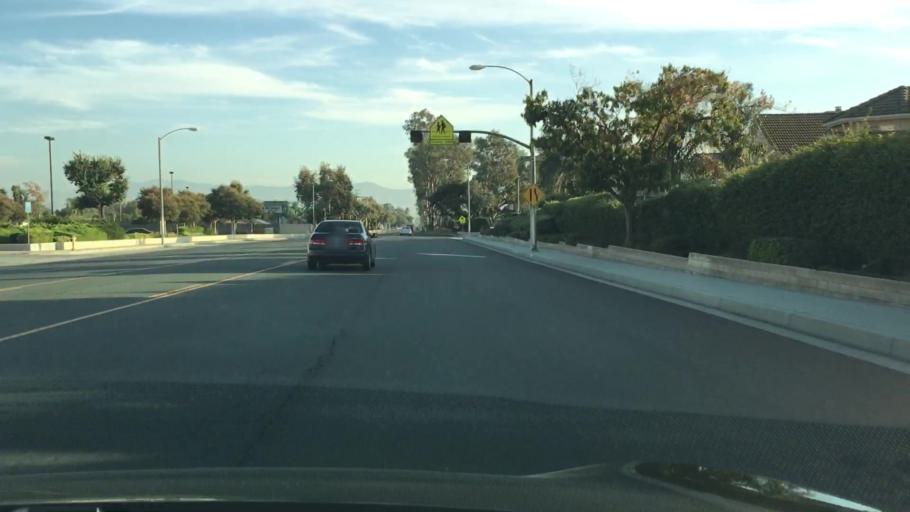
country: US
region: California
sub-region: San Bernardino County
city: Ontario
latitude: 34.0245
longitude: -117.6416
